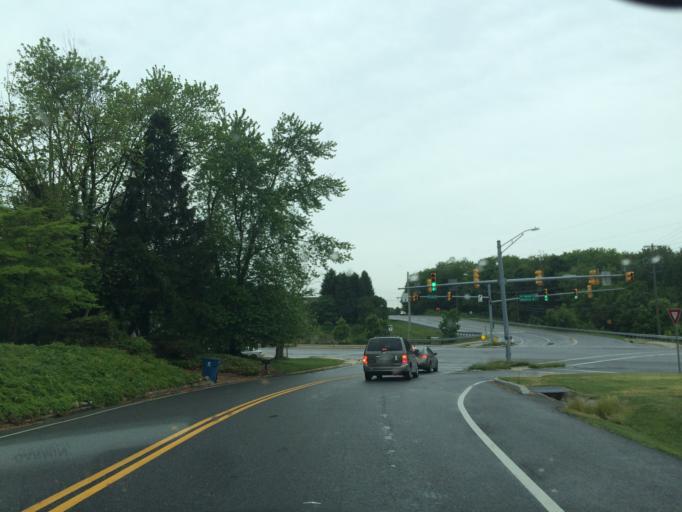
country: US
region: Maryland
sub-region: Washington County
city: Robinwood
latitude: 39.6189
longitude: -77.6836
